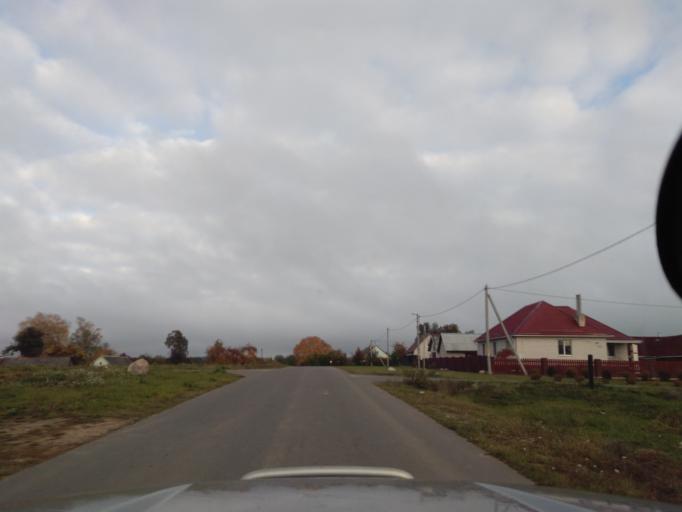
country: BY
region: Minsk
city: Kapyl'
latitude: 53.1605
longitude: 27.0984
